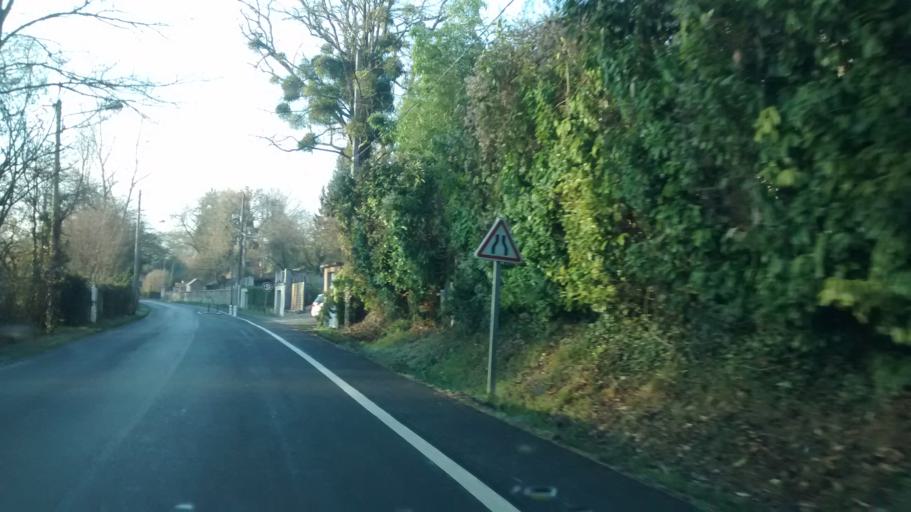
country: FR
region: Centre
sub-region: Departement d'Indre-et-Loire
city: Veigne
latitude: 47.2878
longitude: 0.7296
